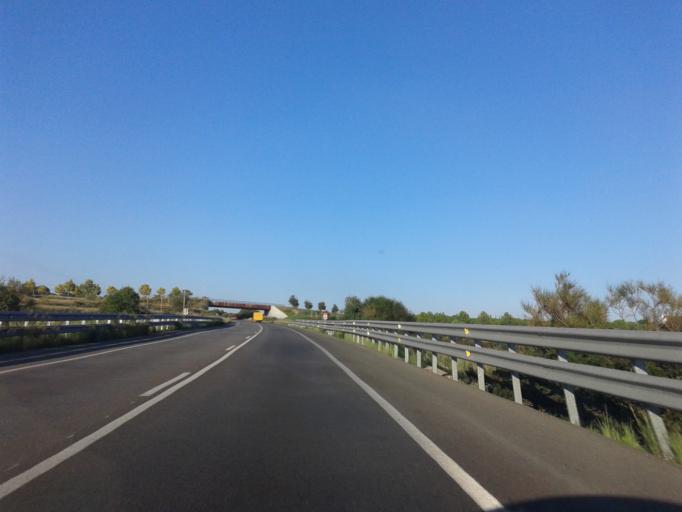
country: ES
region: Catalonia
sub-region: Provincia de Barcelona
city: Cubelles
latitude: 41.2143
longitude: 1.6954
